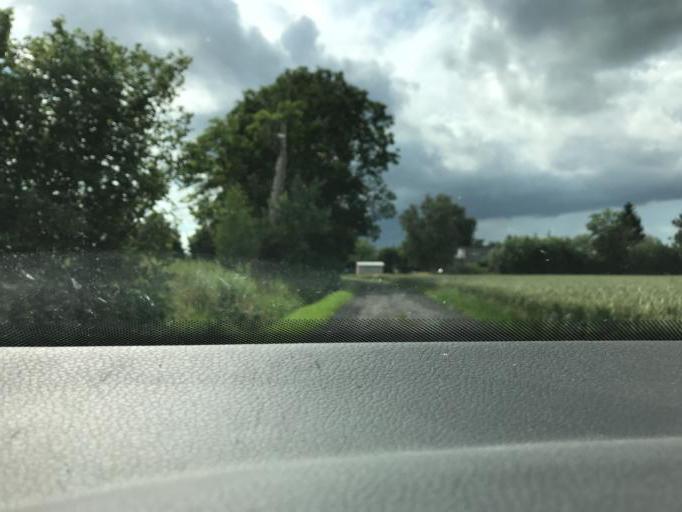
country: PL
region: Pomeranian Voivodeship
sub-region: Powiat gdanski
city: Pruszcz Gdanski
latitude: 54.2954
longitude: 18.7222
